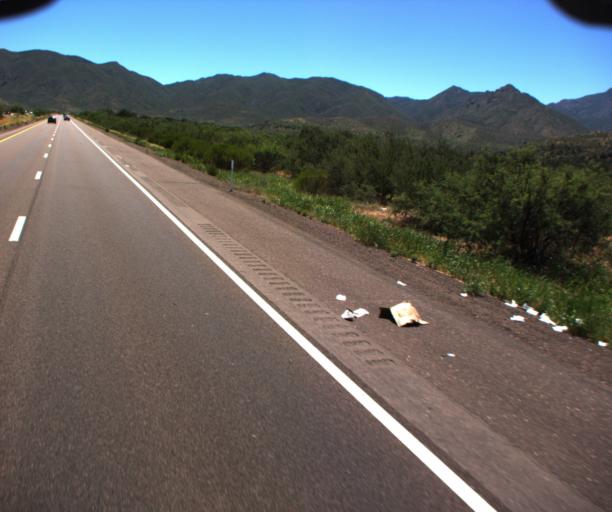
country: US
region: Arizona
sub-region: Gila County
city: Payson
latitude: 34.0548
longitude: -111.3648
